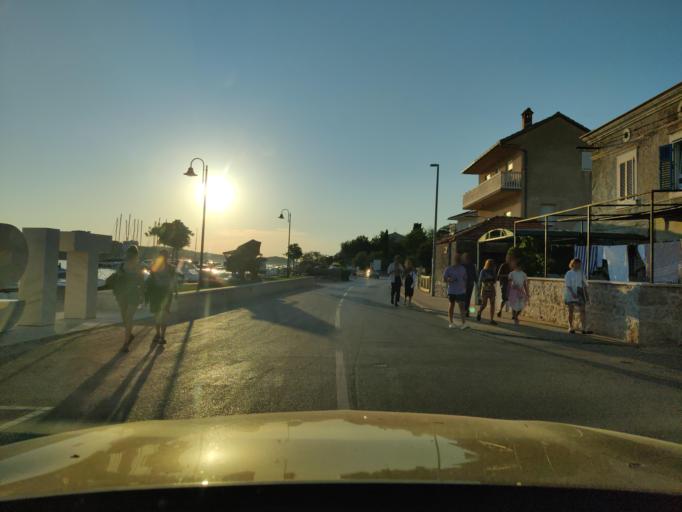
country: HR
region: Sibensko-Kniniska
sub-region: Grad Sibenik
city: Tisno
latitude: 43.8000
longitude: 15.6408
